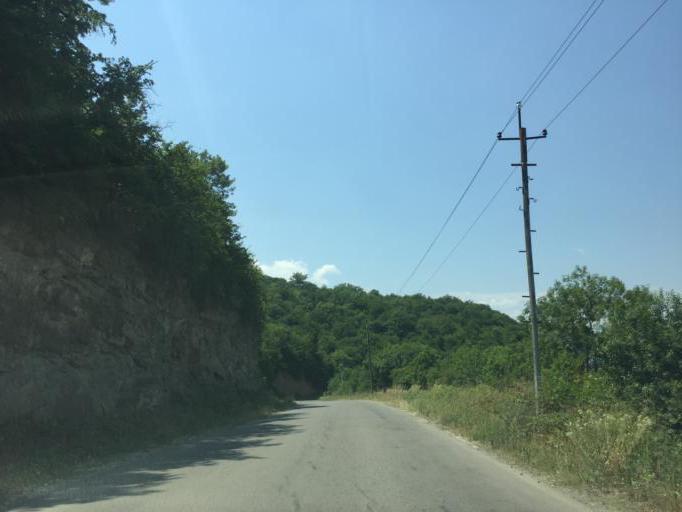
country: AZ
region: Tartar Rayon
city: Martakert
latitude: 40.1371
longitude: 46.4948
